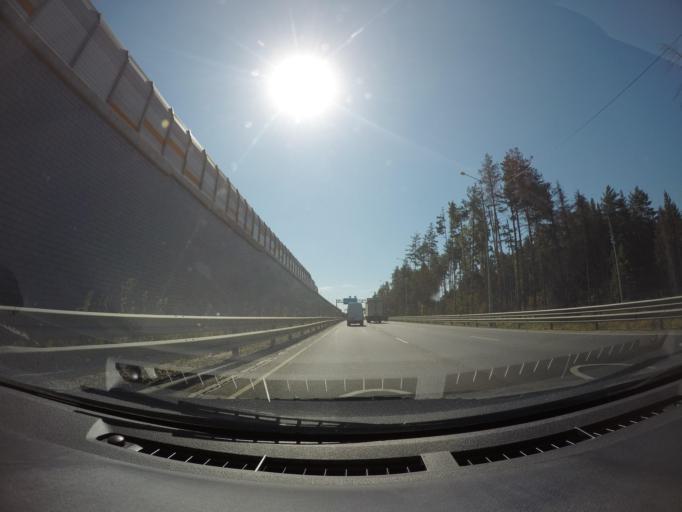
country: RU
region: Moskovskaya
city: Gzhel'
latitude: 55.6263
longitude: 38.3637
